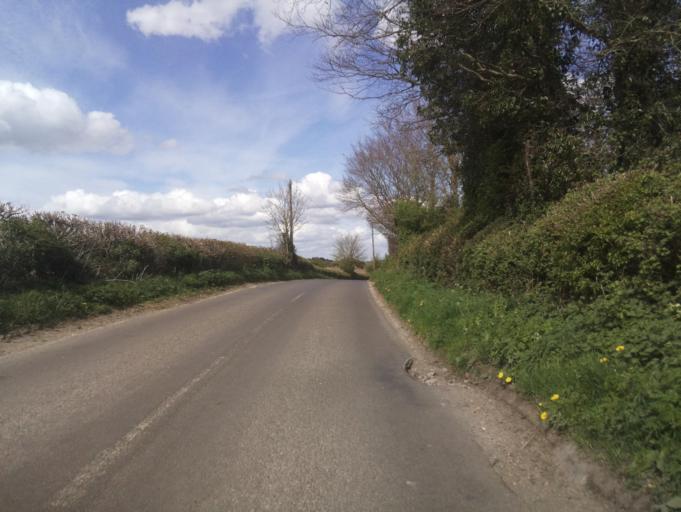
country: GB
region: England
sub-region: Hampshire
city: Abbotts Ann
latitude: 51.0980
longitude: -1.5116
